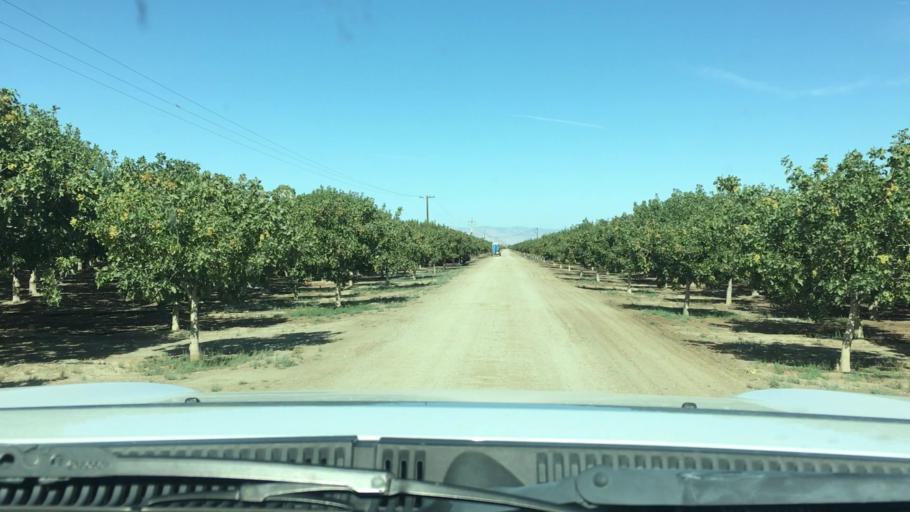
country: US
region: California
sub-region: Kern County
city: Buttonwillow
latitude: 35.3694
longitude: -119.3896
